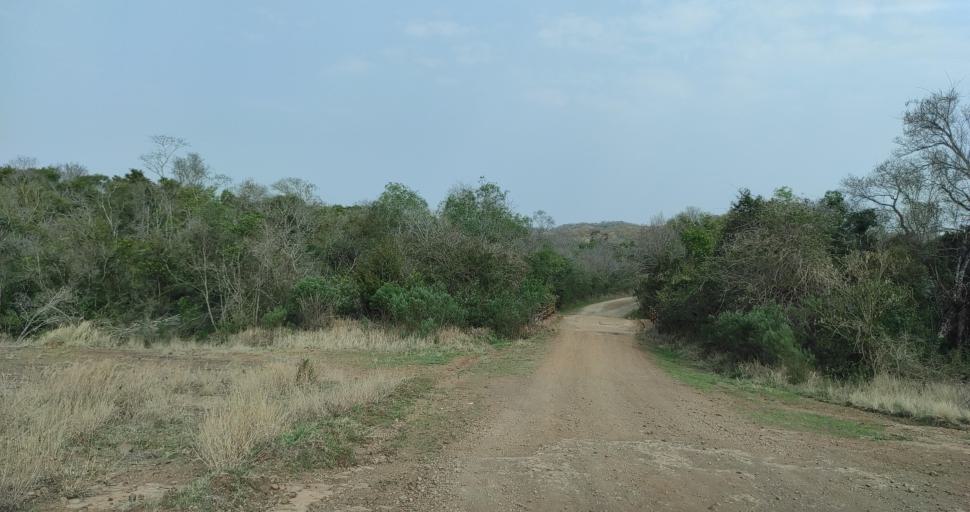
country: AR
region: Misiones
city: Cerro Cora
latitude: -27.5916
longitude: -55.5784
